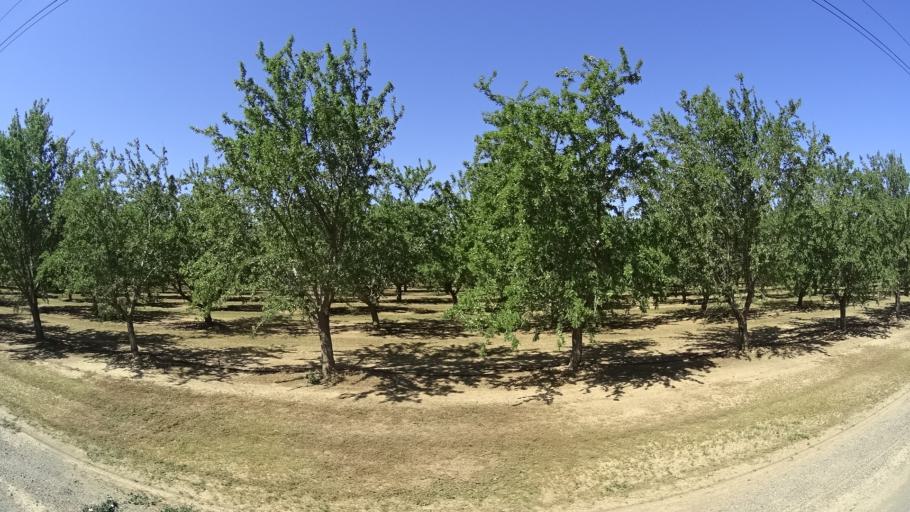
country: US
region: California
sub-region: Glenn County
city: Orland
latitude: 39.7006
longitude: -122.1640
